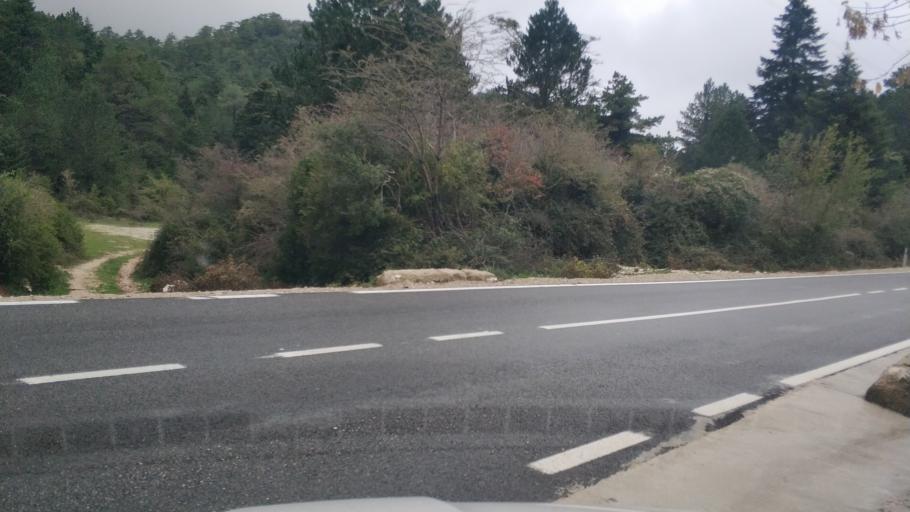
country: AL
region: Vlore
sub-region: Rrethi i Vlores
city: Brataj
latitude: 40.2111
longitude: 19.5791
